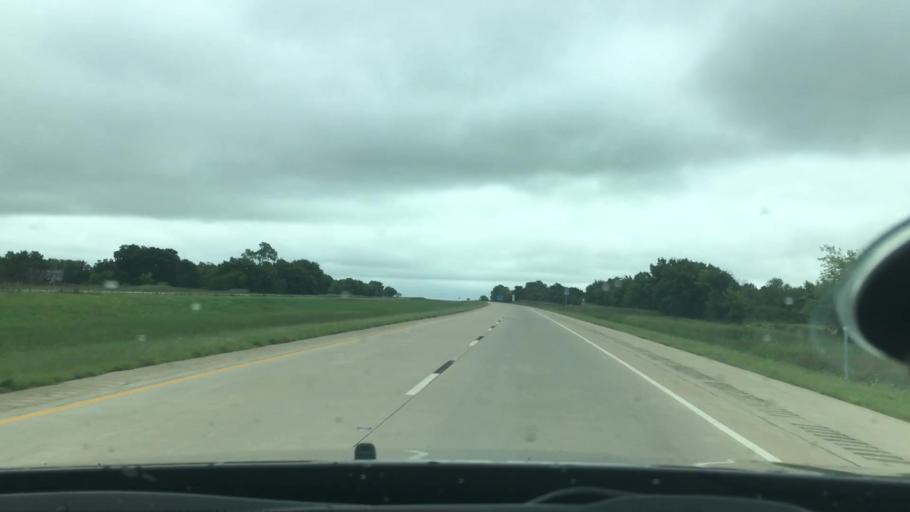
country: US
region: Oklahoma
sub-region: McIntosh County
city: Checotah
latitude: 35.4569
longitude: -95.5859
